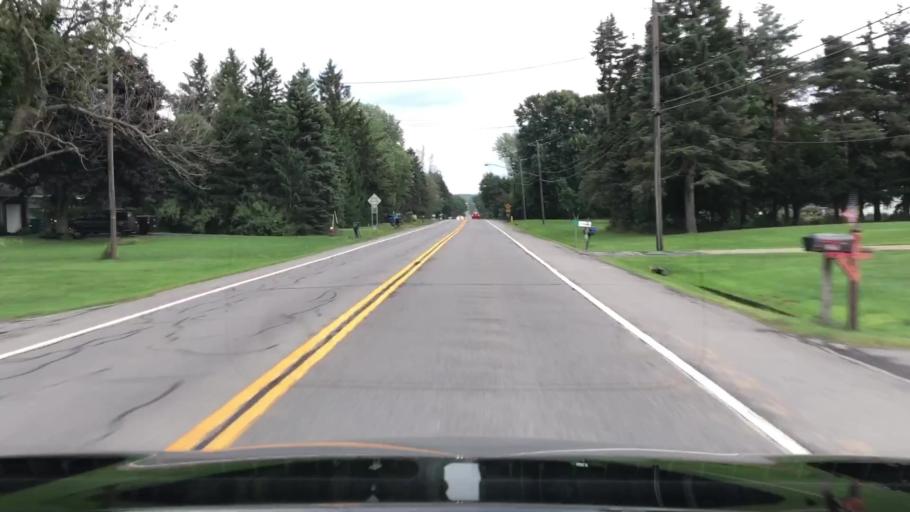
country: US
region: New York
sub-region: Erie County
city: Orchard Park
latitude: 42.7879
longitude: -78.6969
